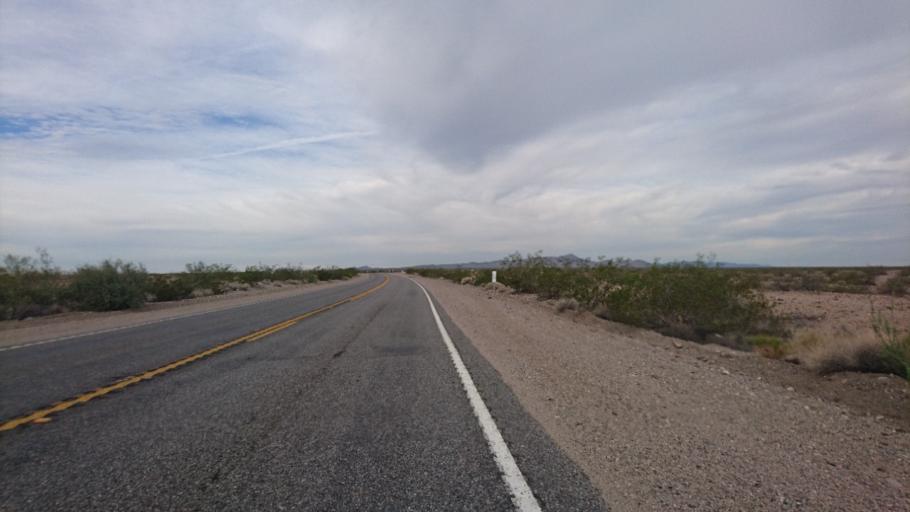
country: US
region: Arizona
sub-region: Mohave County
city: Willow Valley
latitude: 34.9394
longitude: -114.8114
